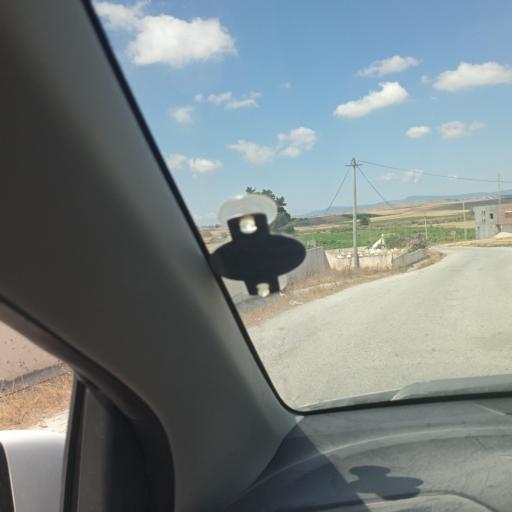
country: TN
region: Nabul
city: Qulaybiyah
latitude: 36.8626
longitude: 11.0295
